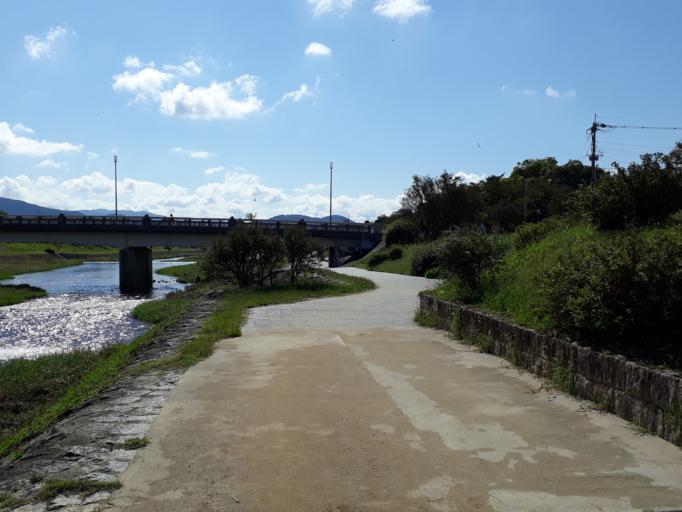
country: JP
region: Kyoto
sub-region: Kyoto-shi
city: Kamigyo-ku
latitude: 35.0389
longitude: 135.7657
